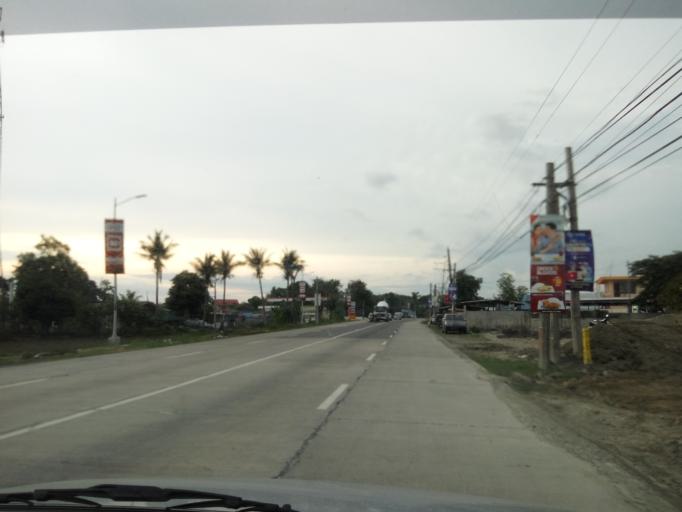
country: PH
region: Ilocos
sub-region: Province of Pangasinan
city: Sison
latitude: 16.1756
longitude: 120.5161
